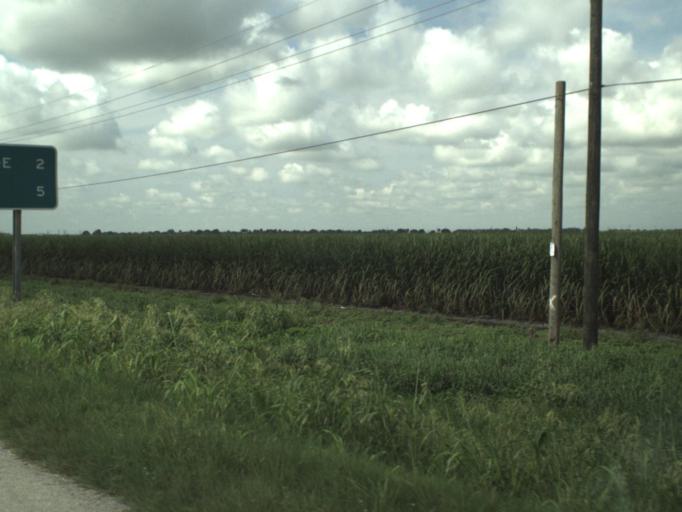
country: US
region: Florida
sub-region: Palm Beach County
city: Belle Glade
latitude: 26.7251
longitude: -80.6841
